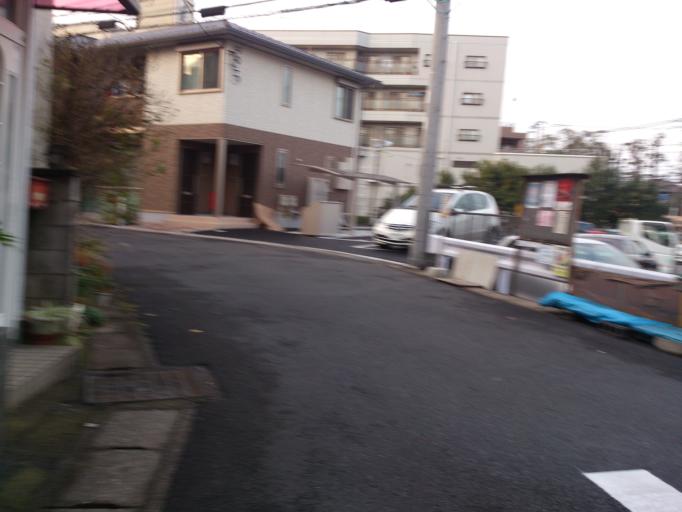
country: JP
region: Chiba
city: Matsudo
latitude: 35.7880
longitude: 139.8970
